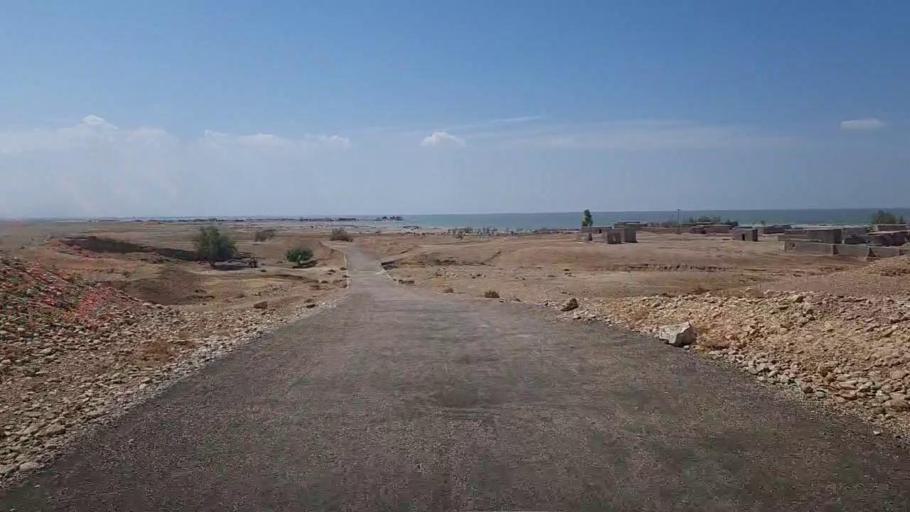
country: PK
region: Sindh
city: Bhan
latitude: 26.3787
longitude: 67.6425
